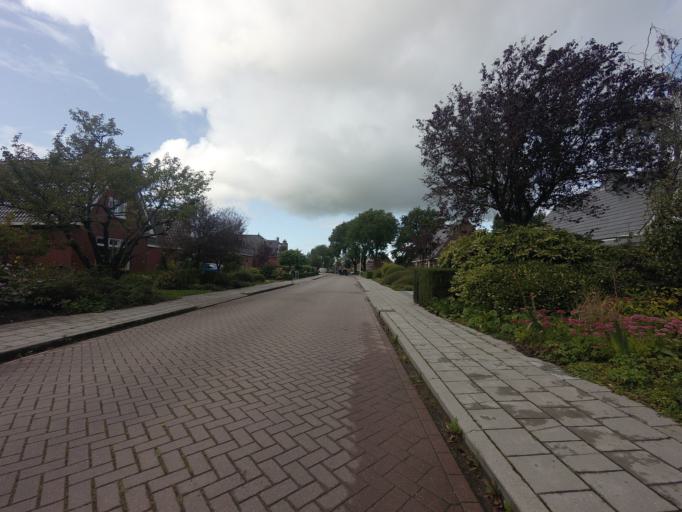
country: NL
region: Friesland
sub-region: Gemeente Boarnsterhim
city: Warten
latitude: 53.1512
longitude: 5.9034
